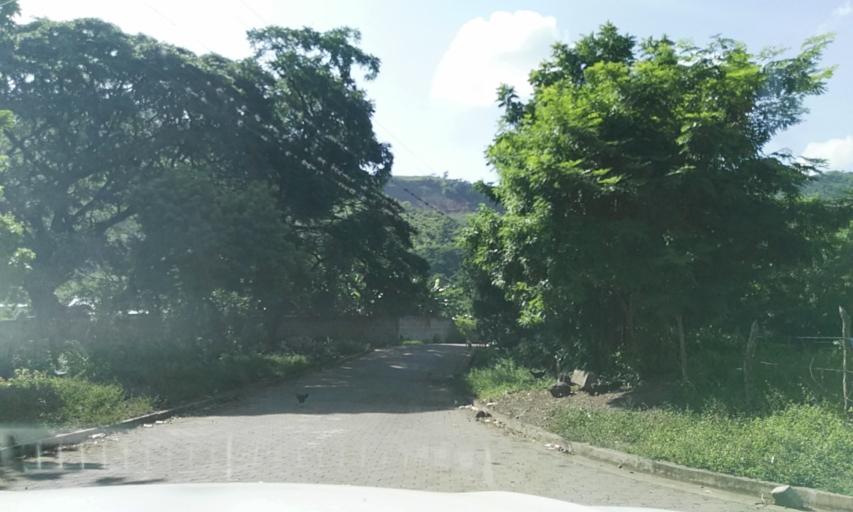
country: NI
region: Matagalpa
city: Terrabona
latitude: 12.7345
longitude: -85.9647
